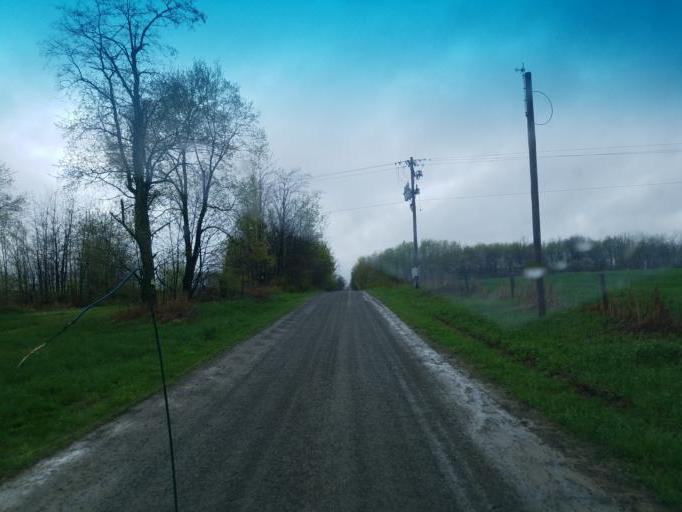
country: US
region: Pennsylvania
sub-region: Tioga County
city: Westfield
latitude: 41.9812
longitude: -77.7074
